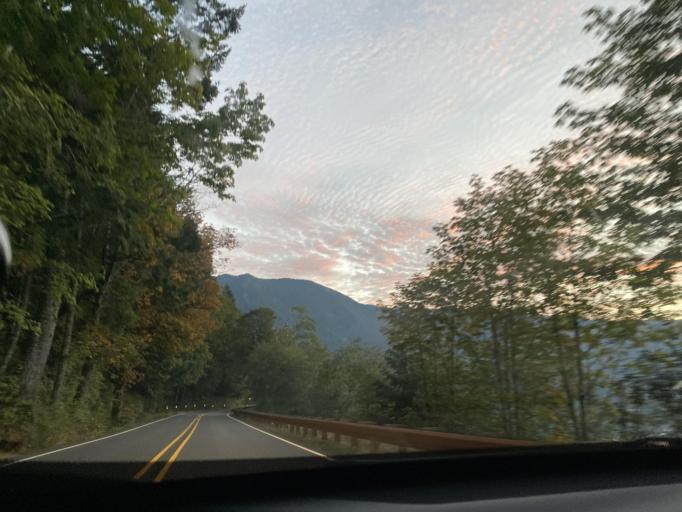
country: CA
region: British Columbia
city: Sooke
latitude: 48.0694
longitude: -123.7745
